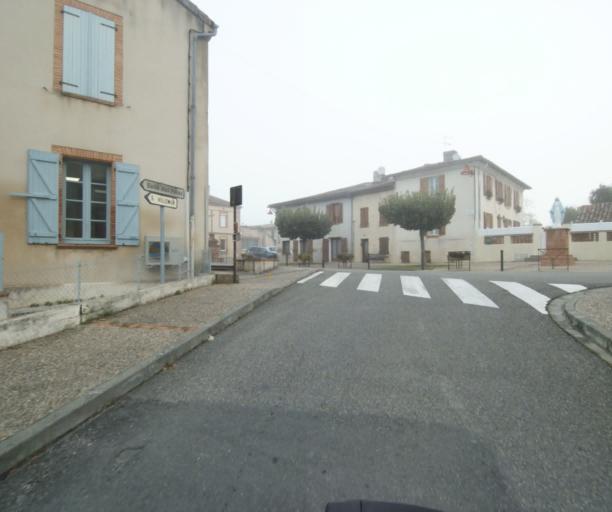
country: FR
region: Midi-Pyrenees
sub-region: Departement du Tarn-et-Garonne
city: Nohic
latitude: 43.9320
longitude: 1.4609
